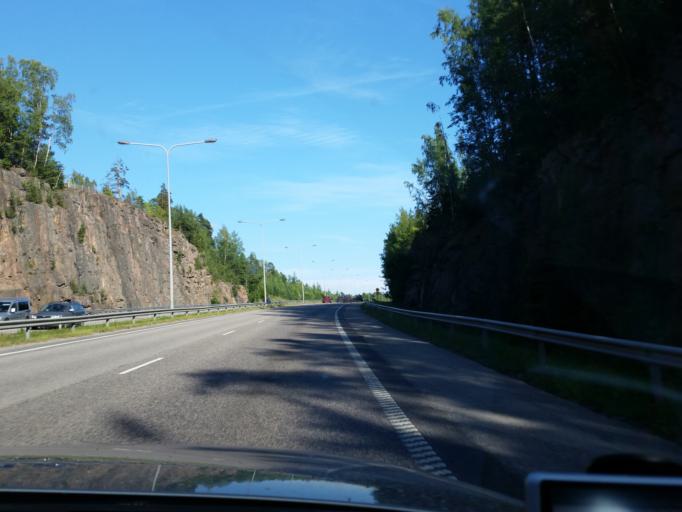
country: FI
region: Uusimaa
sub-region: Helsinki
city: Espoo
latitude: 60.2098
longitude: 24.6828
